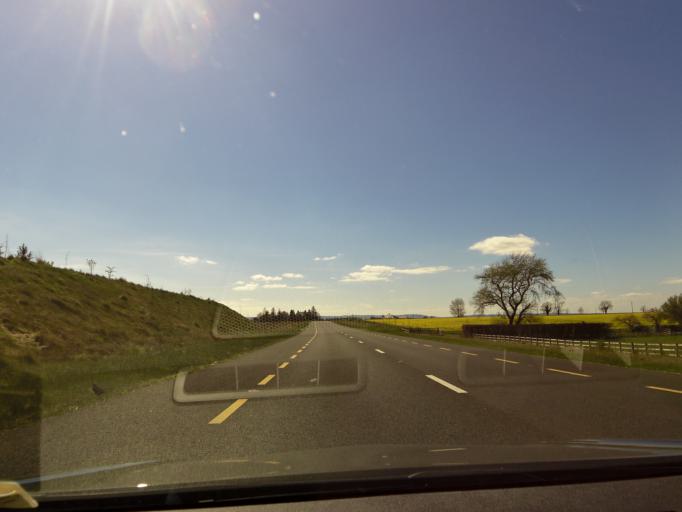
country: IE
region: Leinster
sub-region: Kildare
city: Moone
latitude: 52.9961
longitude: -6.8822
